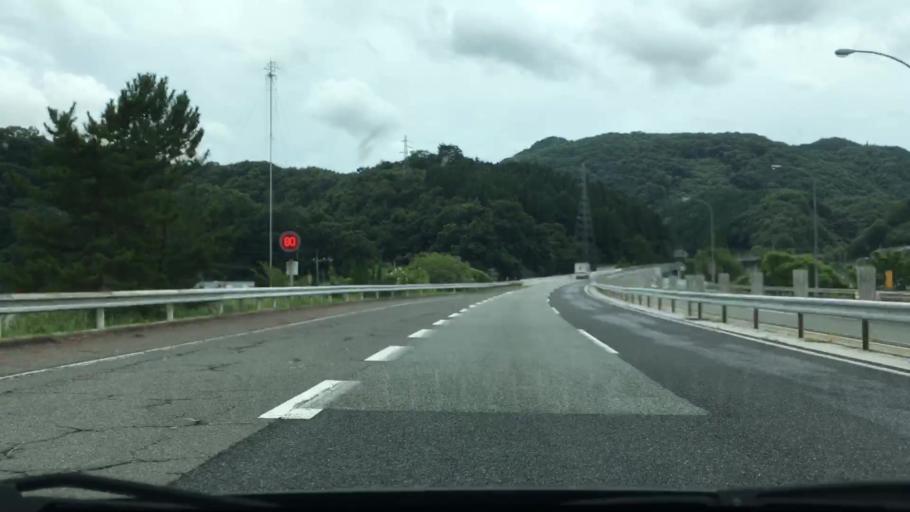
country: JP
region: Okayama
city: Niimi
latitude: 34.8876
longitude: 133.2784
